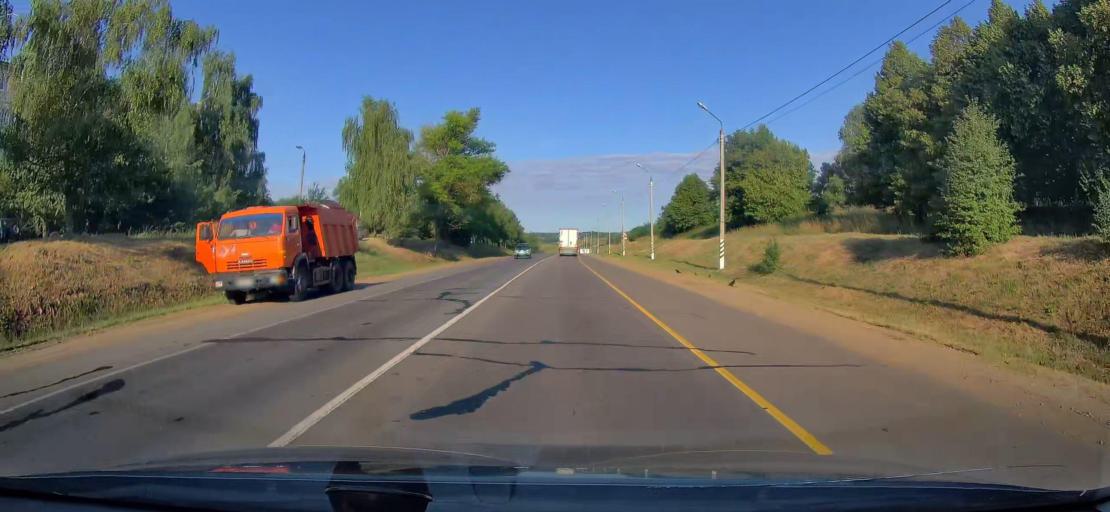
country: RU
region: Tula
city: Chern'
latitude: 53.4552
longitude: 36.9212
